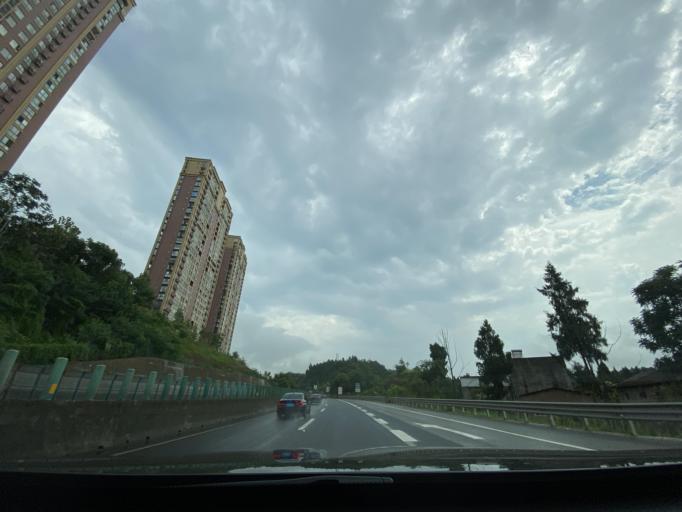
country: CN
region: Sichuan
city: Yanjiang
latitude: 30.1243
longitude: 104.5977
